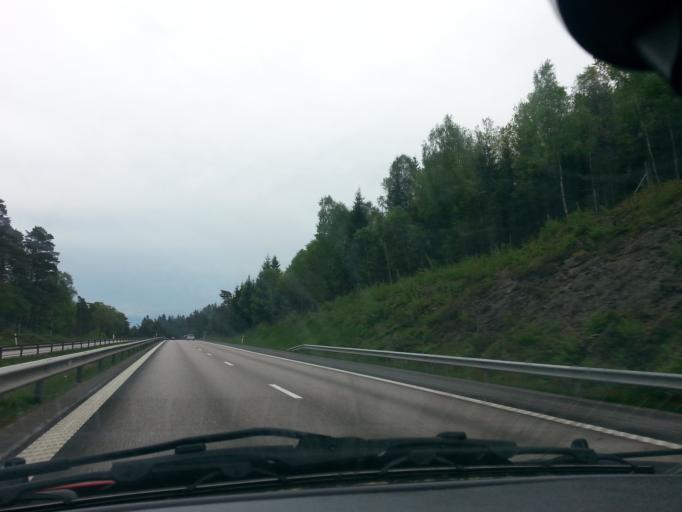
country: SE
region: Vaestra Goetaland
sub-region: Harryda Kommun
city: Landvetter
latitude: 57.7420
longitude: 12.2019
